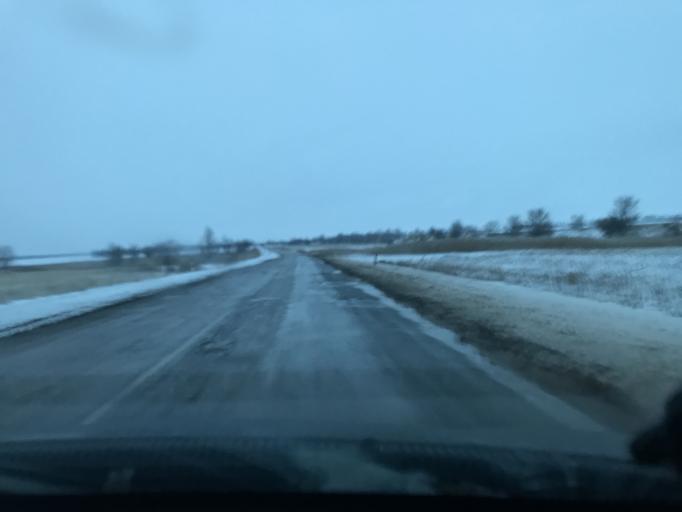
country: RU
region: Rostov
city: Letnik
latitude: 46.0020
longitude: 41.2155
